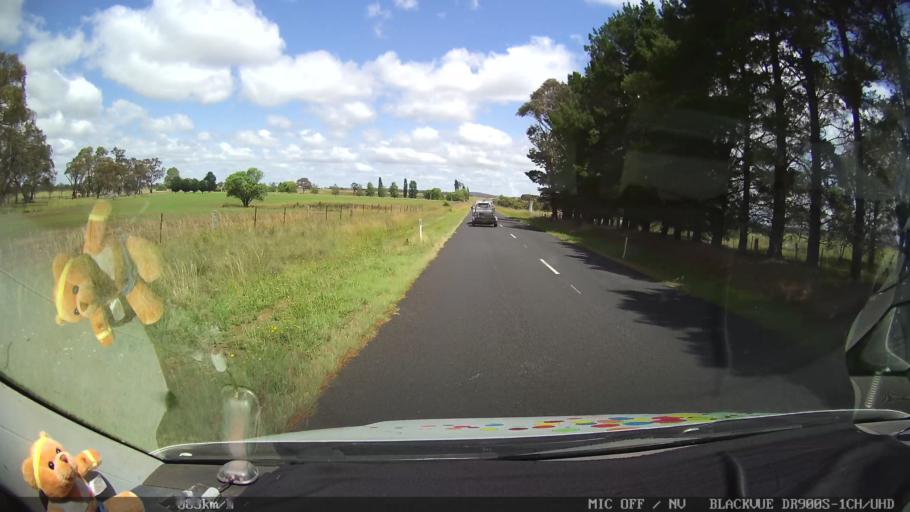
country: AU
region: New South Wales
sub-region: Glen Innes Severn
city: Glen Innes
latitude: -29.6851
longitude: 151.7024
